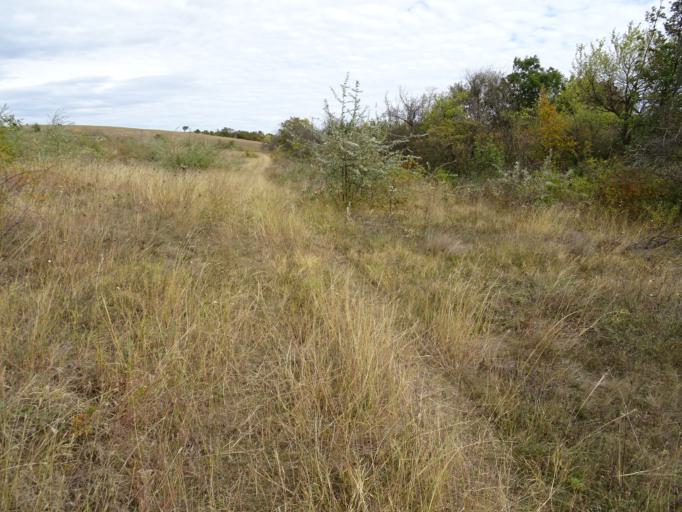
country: HU
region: Fejer
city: Kincsesbanya
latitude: 47.2188
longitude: 18.2545
